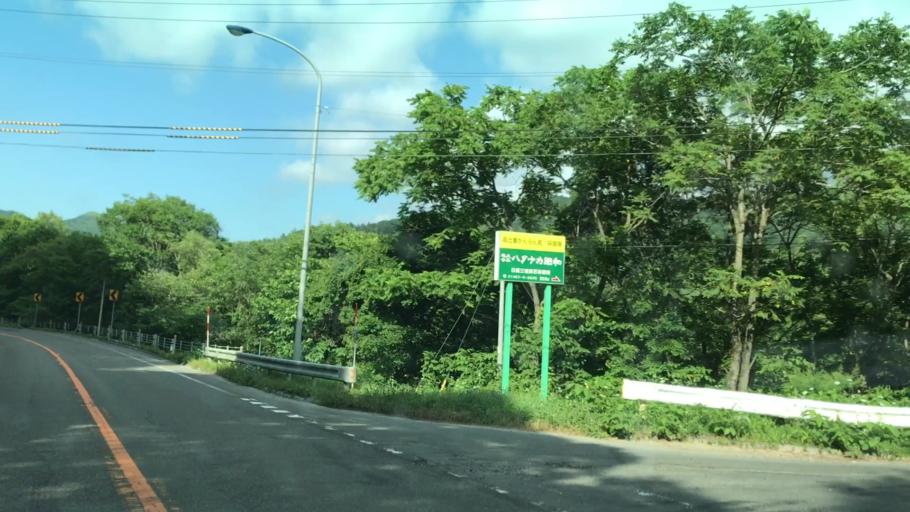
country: JP
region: Hokkaido
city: Shizunai-furukawacho
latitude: 42.7997
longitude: 142.3971
